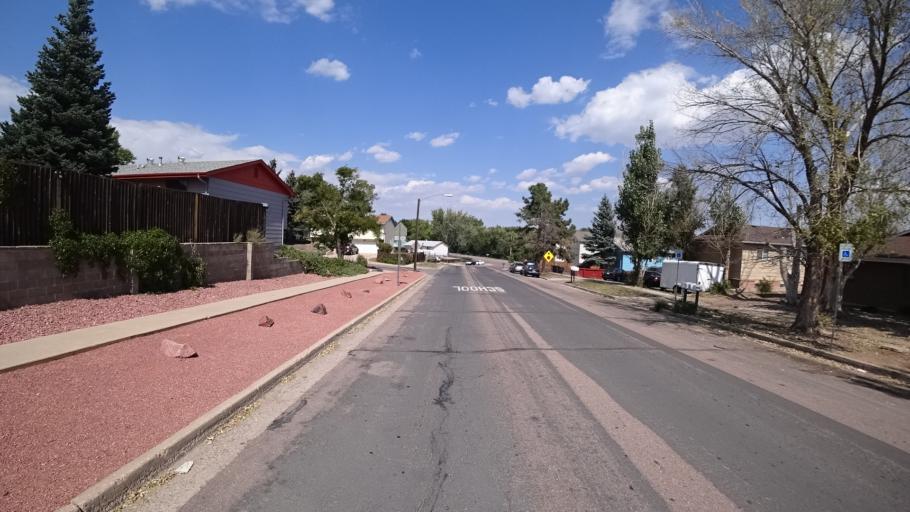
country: US
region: Colorado
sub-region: El Paso County
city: Colorado Springs
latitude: 38.8312
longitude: -104.7627
